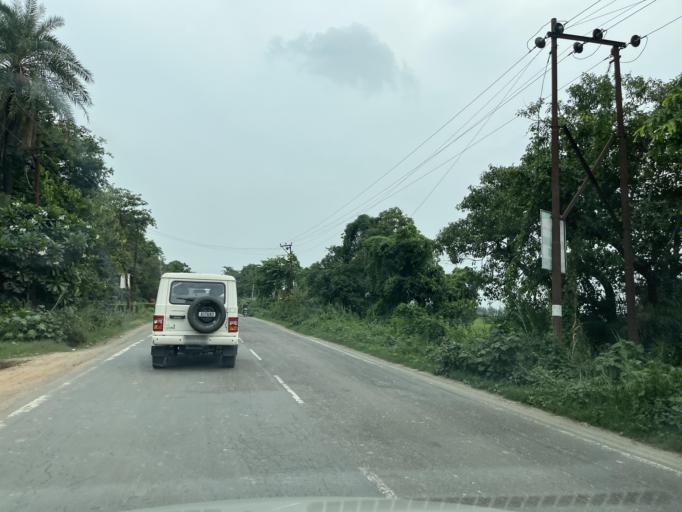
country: IN
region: Uttar Pradesh
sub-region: Rampur
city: Bilaspur
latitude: 29.0262
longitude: 79.2694
